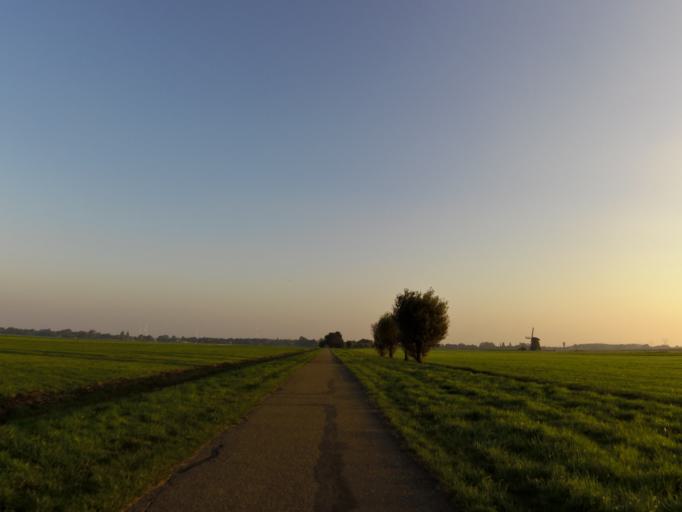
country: NL
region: South Holland
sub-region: Gemeente Leiderdorp
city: Leiderdorp
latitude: 52.1458
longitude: 4.5861
